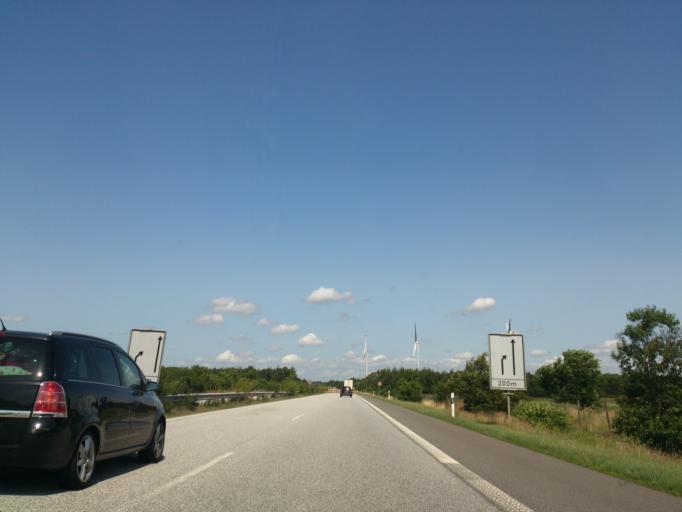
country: DE
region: Schleswig-Holstein
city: Tensbuttel-Rost
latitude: 54.0917
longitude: 9.2664
